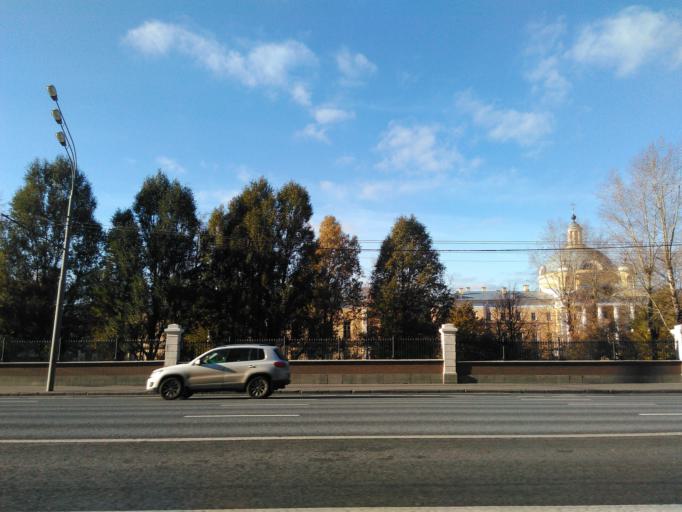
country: RU
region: Moscow
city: Novyye Cheremushki
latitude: 55.7221
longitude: 37.6015
